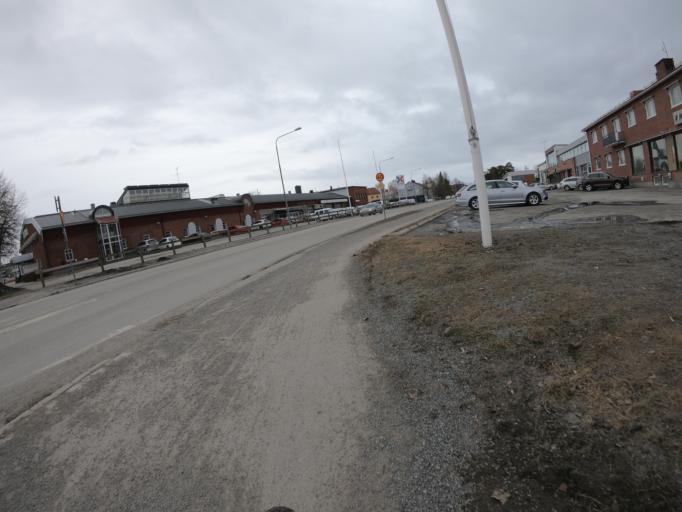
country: SE
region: Vaesterbotten
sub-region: Umea Kommun
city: Umea
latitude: 63.8327
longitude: 20.2822
